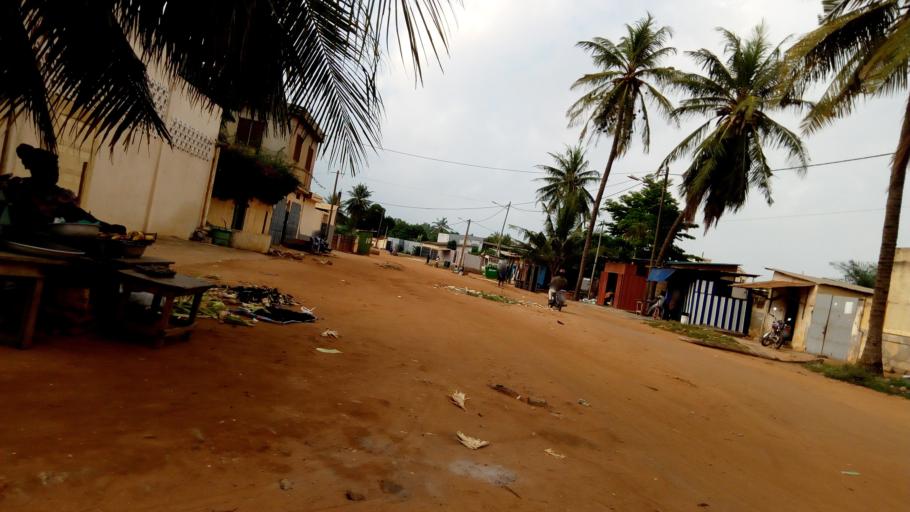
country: TG
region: Maritime
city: Lome
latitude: 6.1784
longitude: 1.1928
